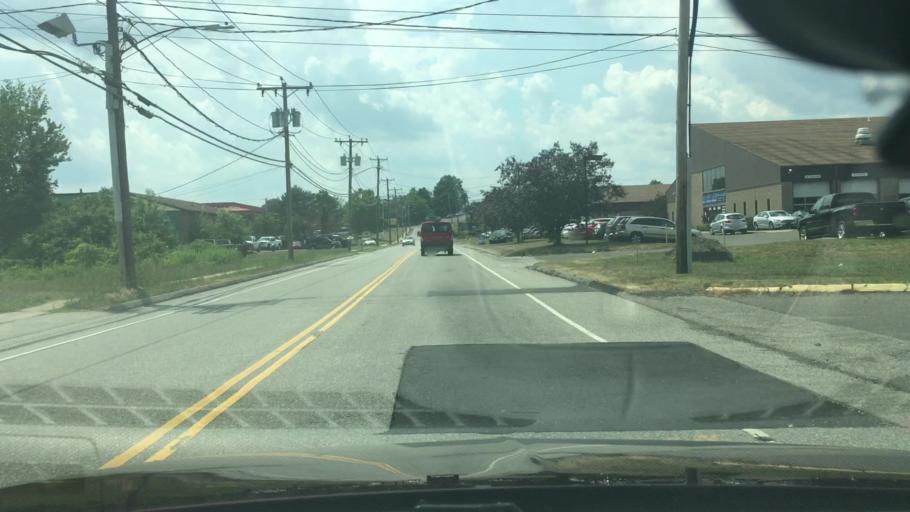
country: US
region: Connecticut
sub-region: Hartford County
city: Kensington
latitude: 41.6542
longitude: -72.7467
